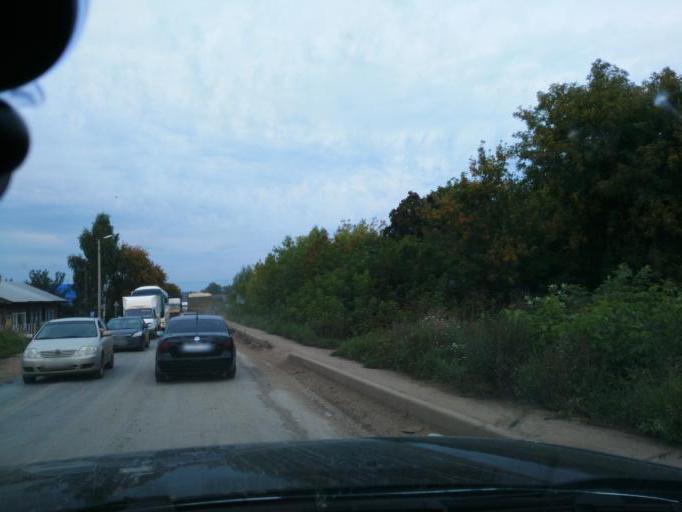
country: RU
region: Perm
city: Kuyeda
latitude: 56.4248
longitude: 55.5821
